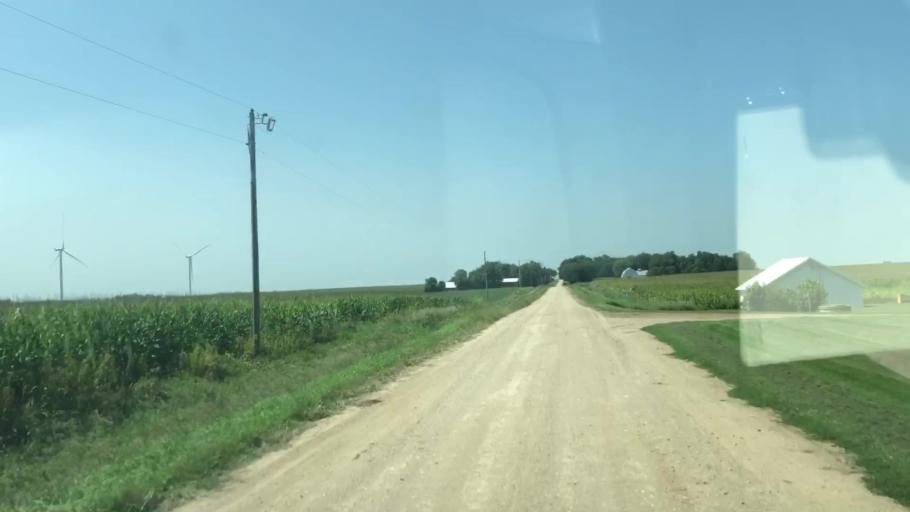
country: US
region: Iowa
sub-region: O'Brien County
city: Sanborn
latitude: 43.2006
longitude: -95.7116
